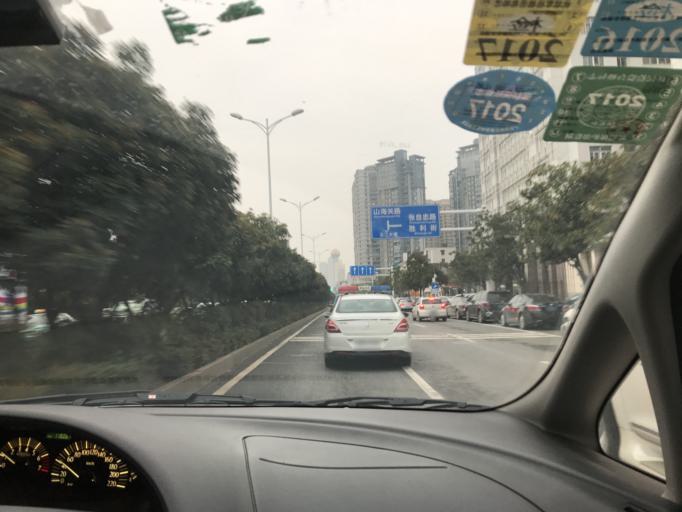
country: CN
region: Hubei
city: Jiang'an
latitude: 30.6072
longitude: 114.3075
